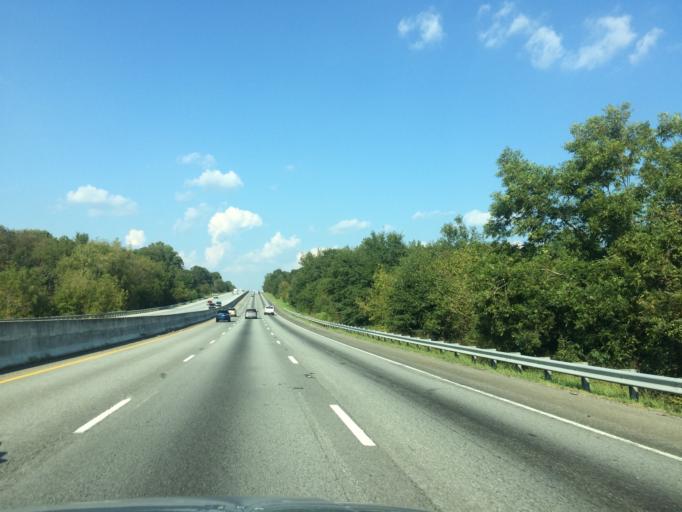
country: US
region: South Carolina
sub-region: Anderson County
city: Williamston
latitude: 34.6504
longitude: -82.5710
